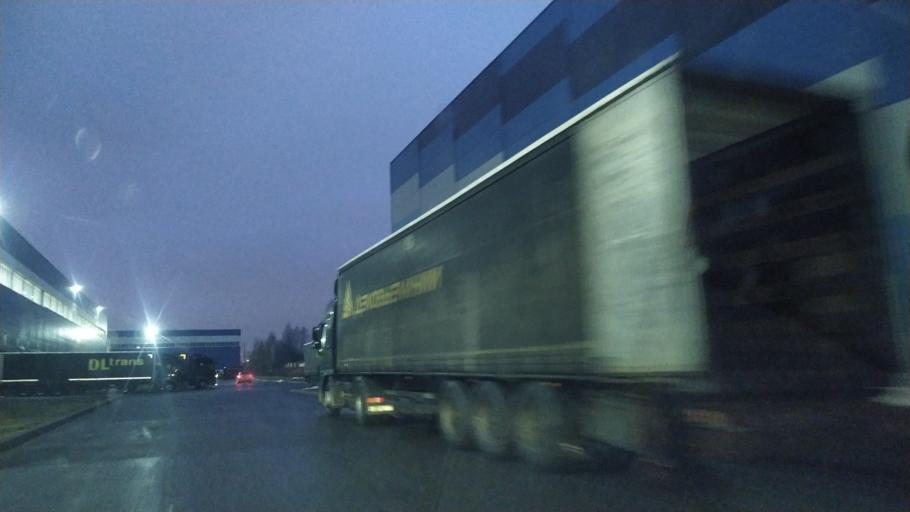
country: RU
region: Leningrad
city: Bugry
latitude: 60.0640
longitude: 30.3815
